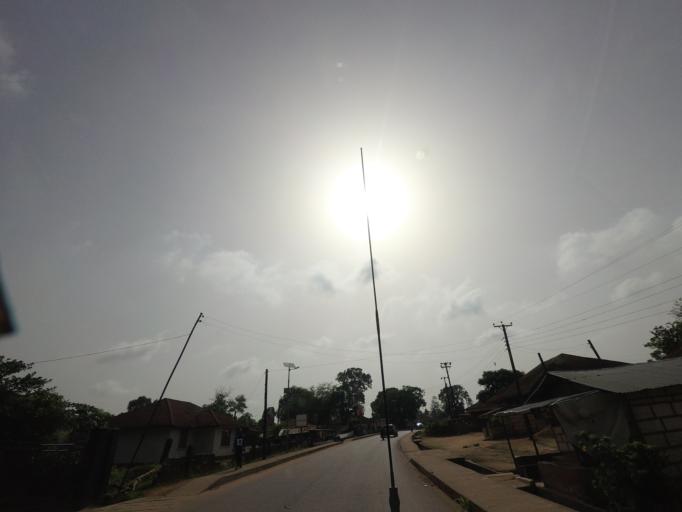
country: SL
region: Southern Province
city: Bo
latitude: 7.9582
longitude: -11.7493
